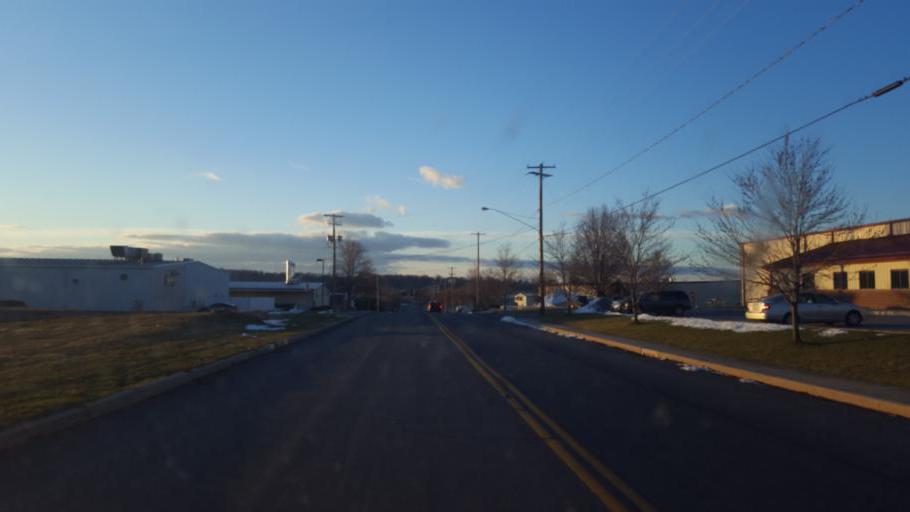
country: US
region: Pennsylvania
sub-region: Lancaster County
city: New Holland
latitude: 40.0933
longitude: -76.0903
